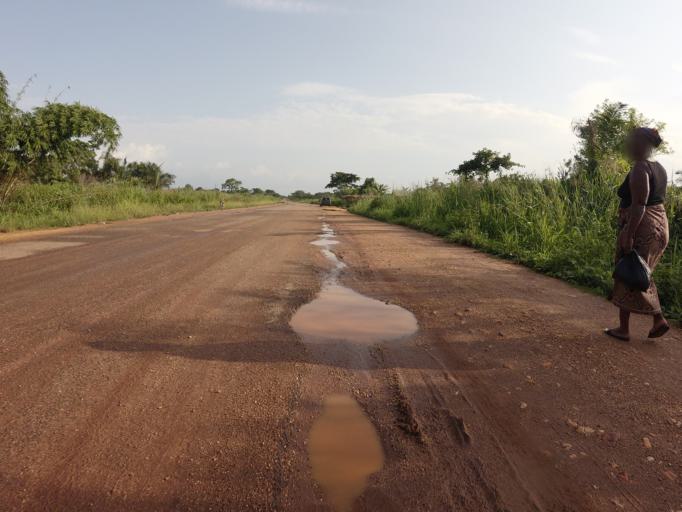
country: GH
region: Volta
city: Hohoe
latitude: 7.0727
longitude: 0.4360
